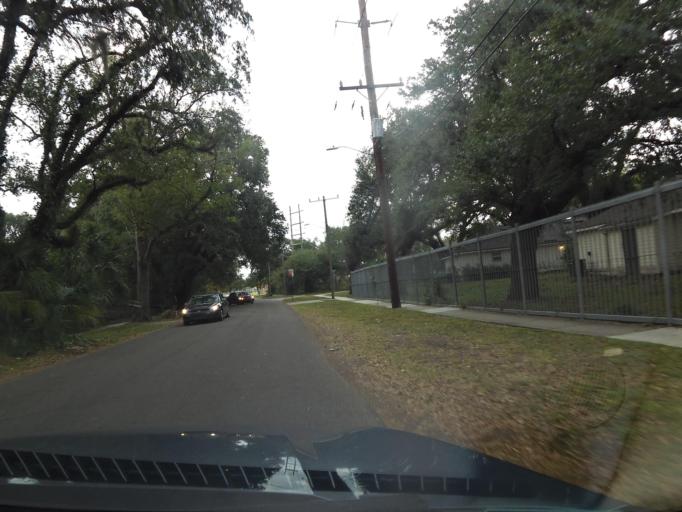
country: US
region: Florida
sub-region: Duval County
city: Jacksonville
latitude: 30.3625
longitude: -81.6659
